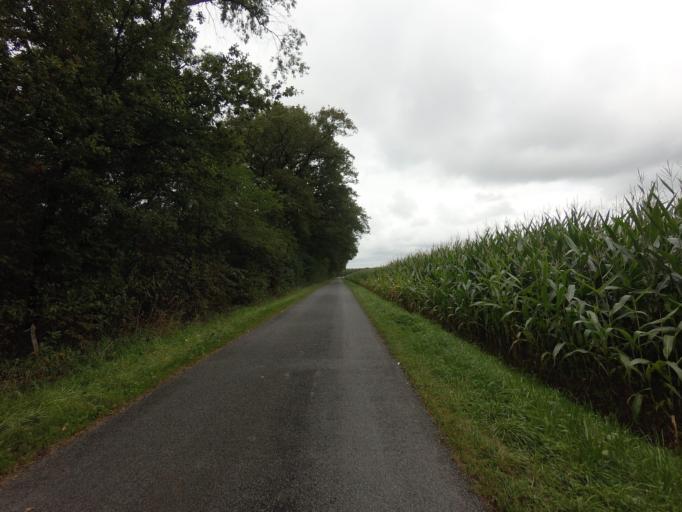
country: DE
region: North Rhine-Westphalia
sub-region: Regierungsbezirk Munster
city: Gronau
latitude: 52.2517
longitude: 7.0804
